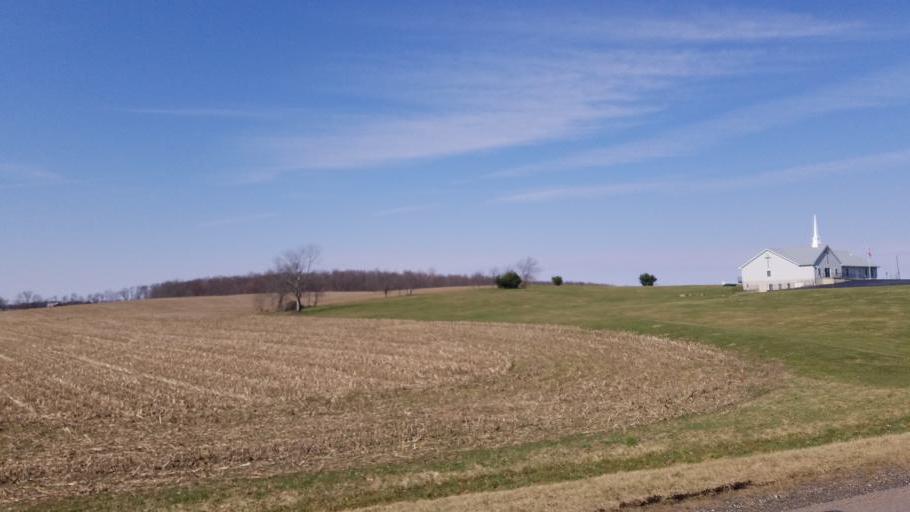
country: US
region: Ohio
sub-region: Knox County
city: Fredericktown
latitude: 40.5198
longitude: -82.5488
